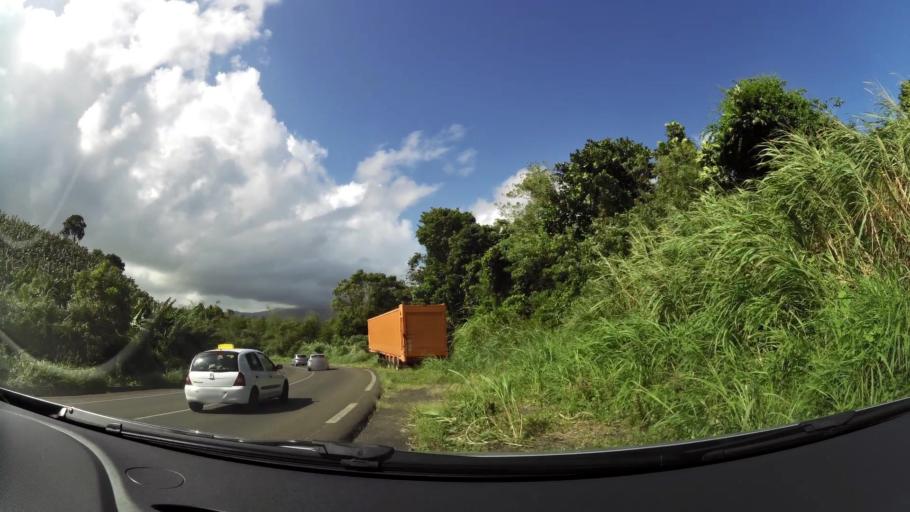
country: MQ
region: Martinique
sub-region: Martinique
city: Le Lorrain
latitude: 14.8434
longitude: -61.0897
